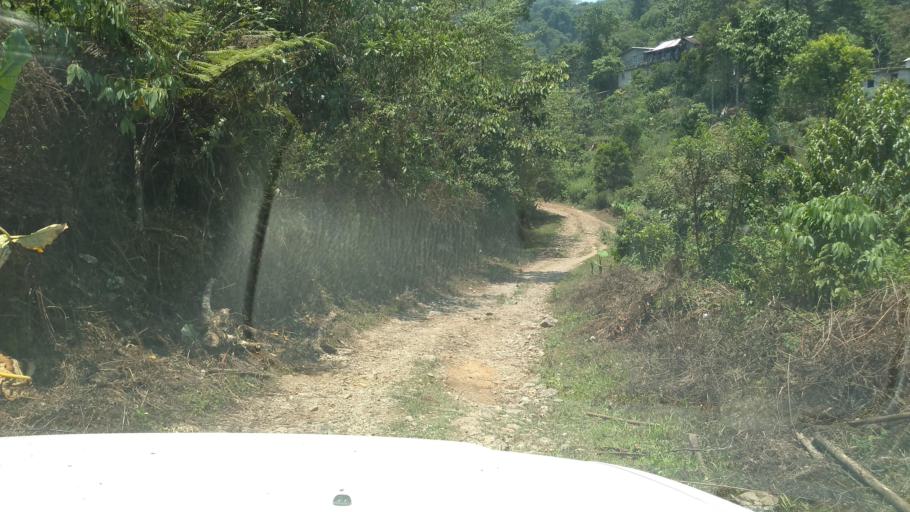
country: MX
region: Veracruz
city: Motzorongo
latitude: 18.6120
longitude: -96.7618
